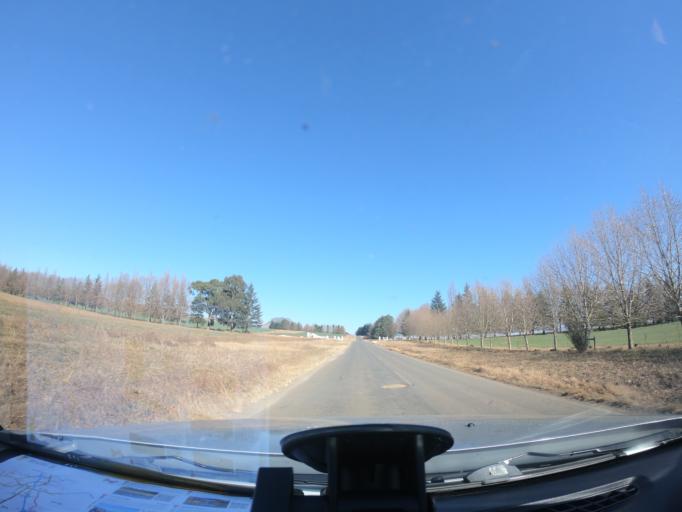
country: ZA
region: KwaZulu-Natal
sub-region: uMgungundlovu District Municipality
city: Mooirivier
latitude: -29.3265
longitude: 29.8288
